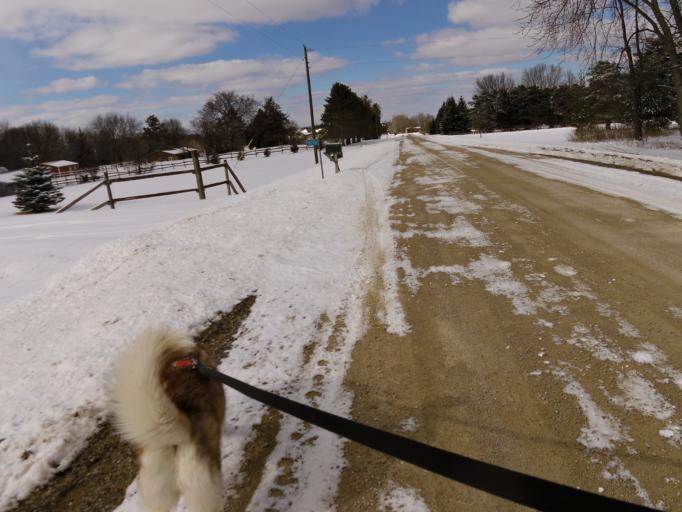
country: US
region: Minnesota
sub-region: Scott County
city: Prior Lake
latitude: 44.6855
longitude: -93.4527
